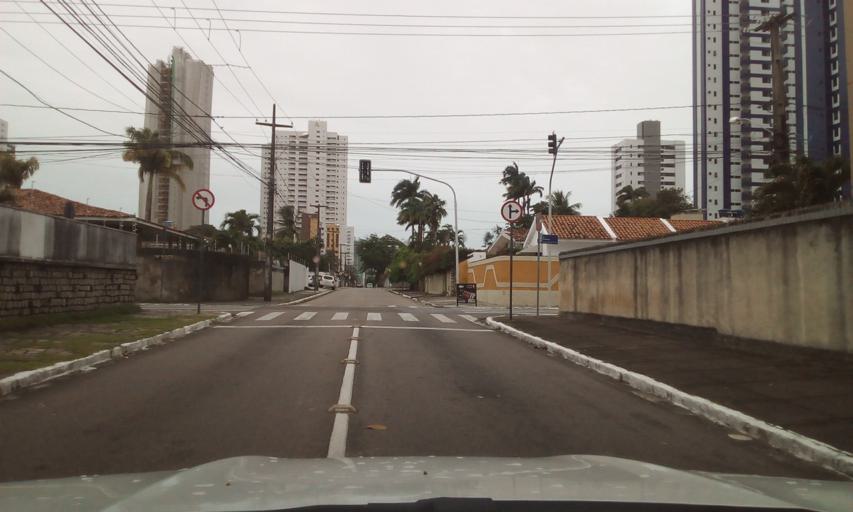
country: BR
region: Paraiba
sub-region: Joao Pessoa
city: Joao Pessoa
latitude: -7.1146
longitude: -34.8556
